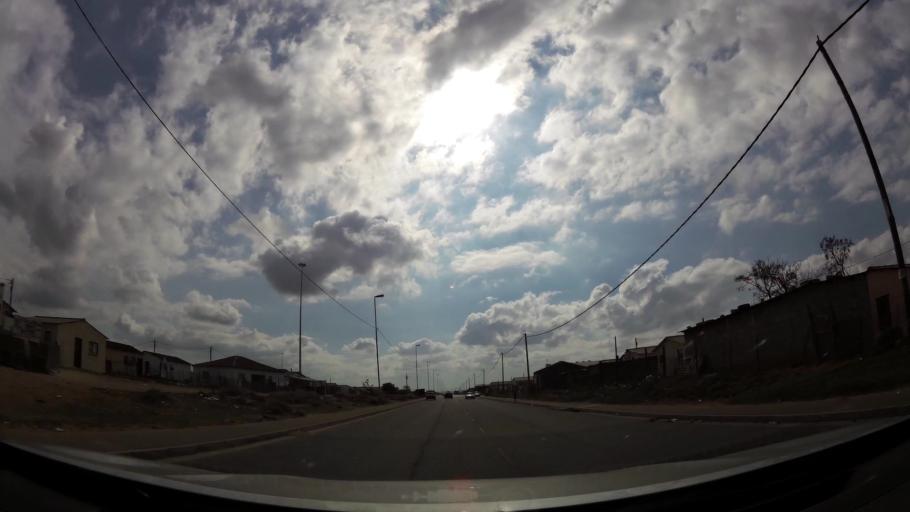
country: ZA
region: Eastern Cape
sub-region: Nelson Mandela Bay Metropolitan Municipality
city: Port Elizabeth
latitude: -33.7945
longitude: 25.5822
